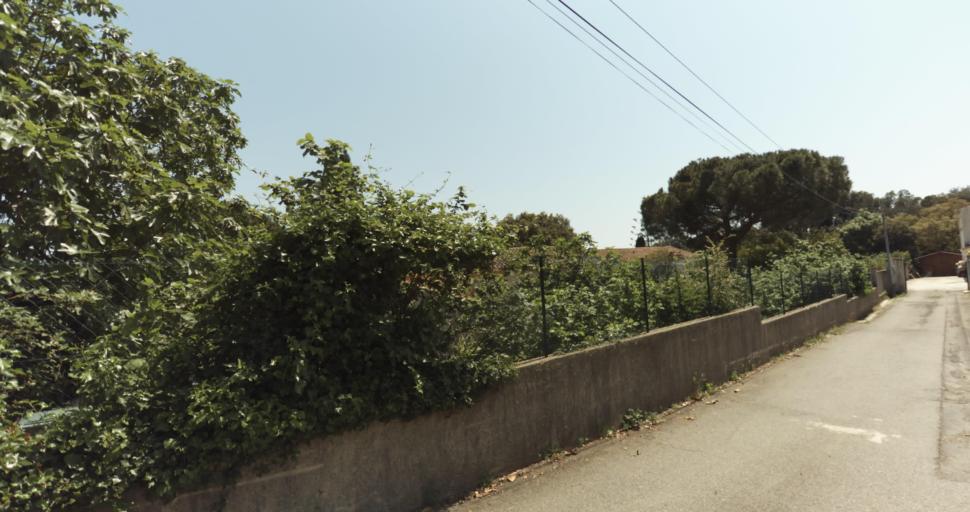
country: FR
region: Corsica
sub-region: Departement de la Haute-Corse
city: Biguglia
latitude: 42.5906
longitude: 9.4282
